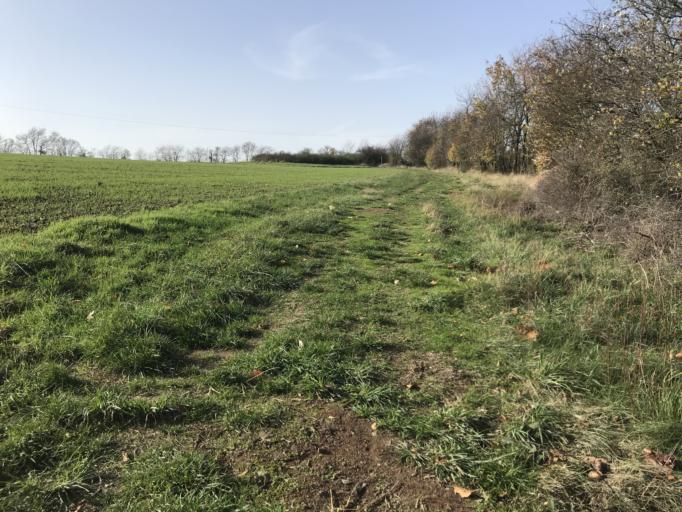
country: DE
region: Rheinland-Pfalz
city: Bacharach
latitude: 50.0660
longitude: 7.7571
